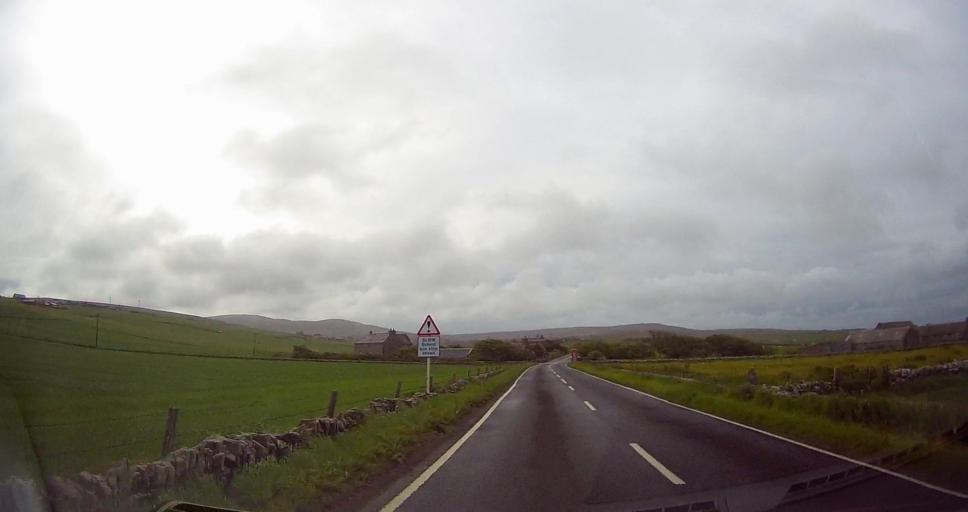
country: GB
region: Scotland
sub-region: Orkney Islands
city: Stromness
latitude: 58.9698
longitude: -3.2310
